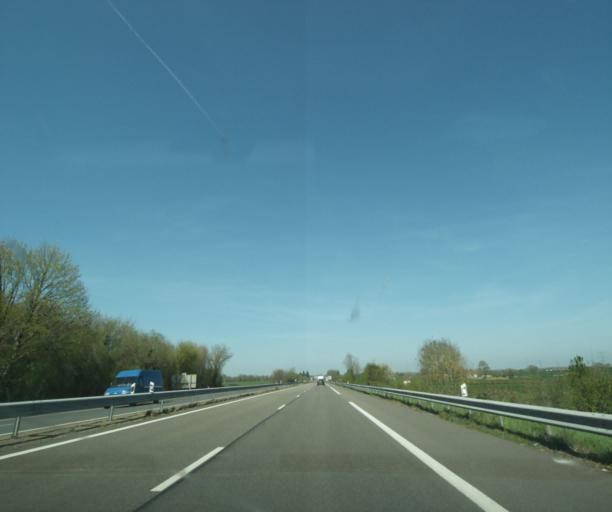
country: FR
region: Bourgogne
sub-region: Departement de la Nievre
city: La Charite-sur-Loire
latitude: 47.1768
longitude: 3.0438
